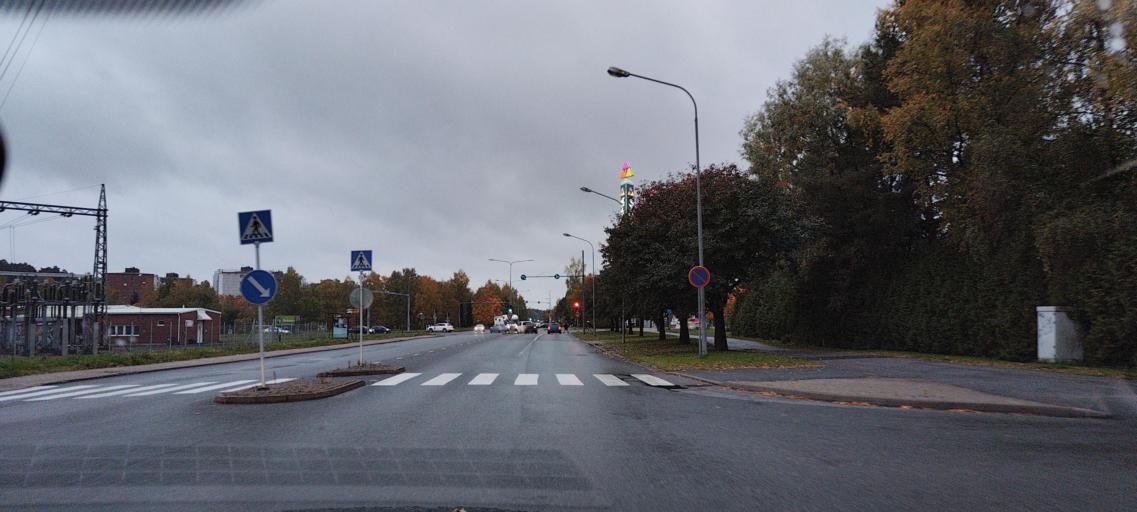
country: FI
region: Varsinais-Suomi
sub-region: Turku
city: Kaarina
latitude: 60.4469
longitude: 22.3280
